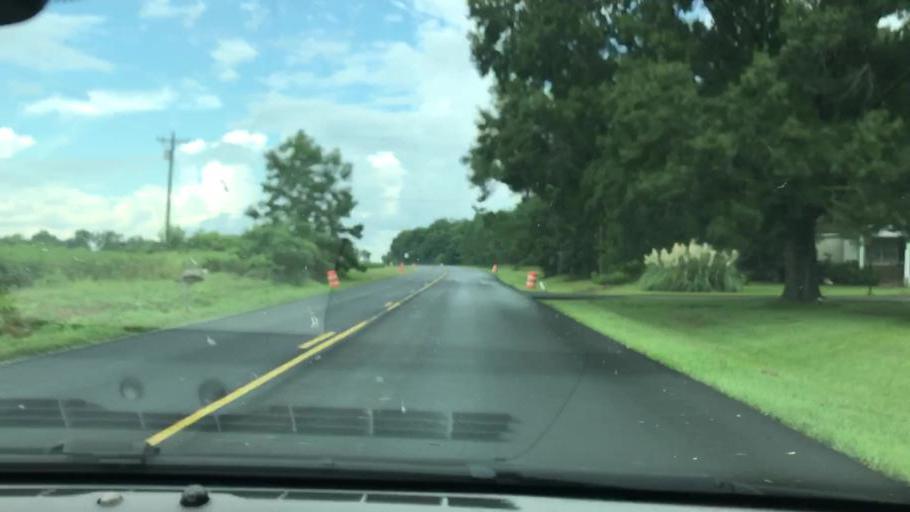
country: US
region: Georgia
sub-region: Early County
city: Blakely
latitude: 31.4325
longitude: -84.9726
